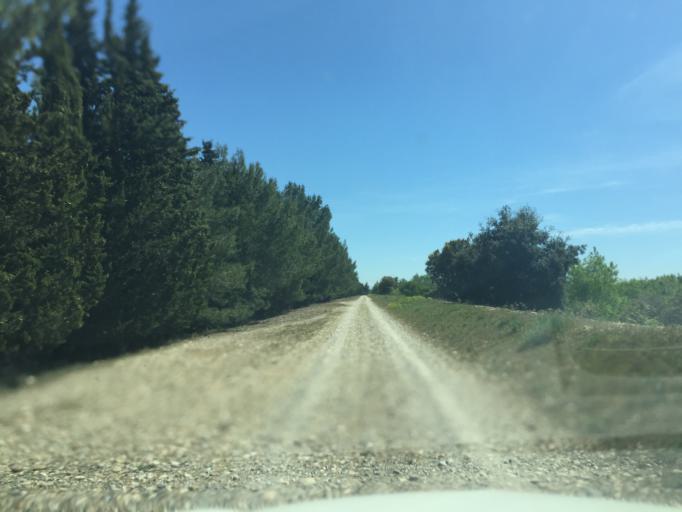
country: FR
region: Languedoc-Roussillon
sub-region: Departement du Gard
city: Roquemaure
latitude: 44.0519
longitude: 4.7935
